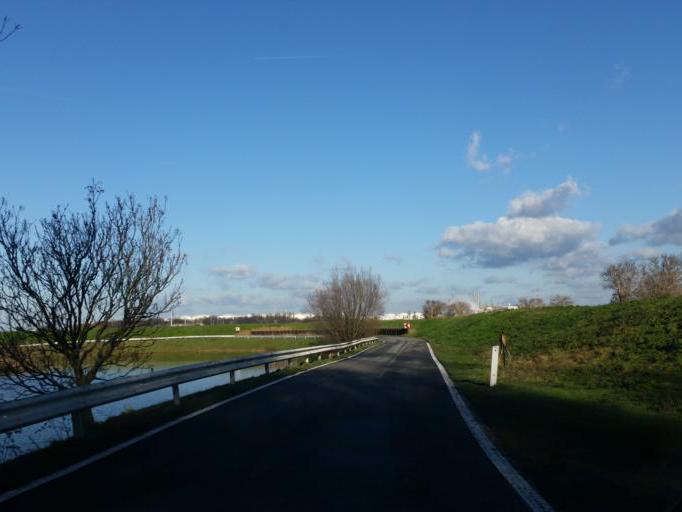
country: BE
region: Flanders
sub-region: Provincie Antwerpen
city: Zwijndrecht
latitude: 51.2939
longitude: 4.2874
